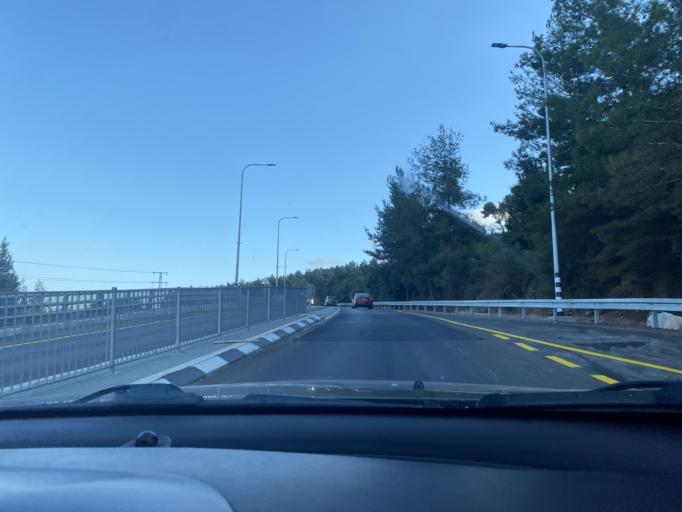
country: IL
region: Northern District
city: Kefar Weradim
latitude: 33.0006
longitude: 35.2820
